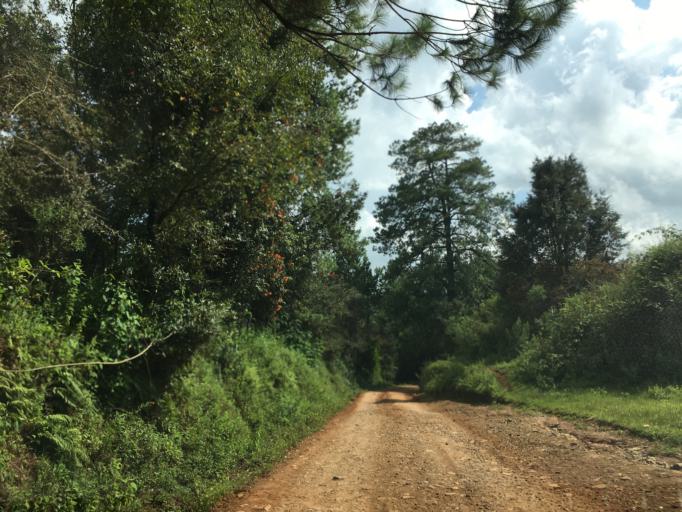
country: MX
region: Michoacan
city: Acuitzio del Canje
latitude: 19.5231
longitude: -101.2089
